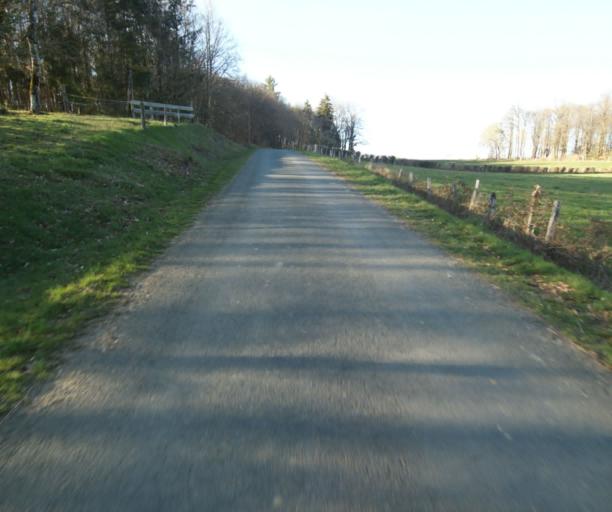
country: FR
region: Limousin
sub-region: Departement de la Correze
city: Seilhac
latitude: 45.3575
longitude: 1.7006
